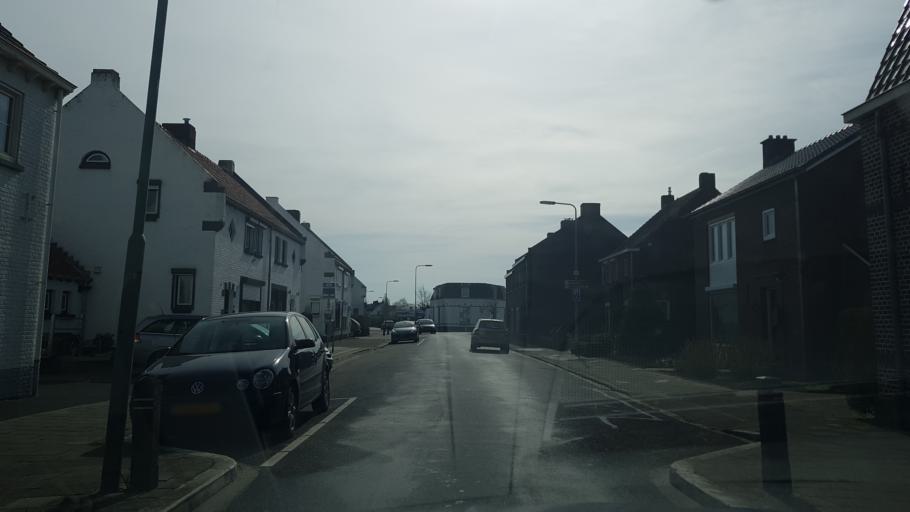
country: NL
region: Limburg
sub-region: Gemeente Leudal
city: Kelpen-Oler
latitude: 51.1649
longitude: 5.8364
